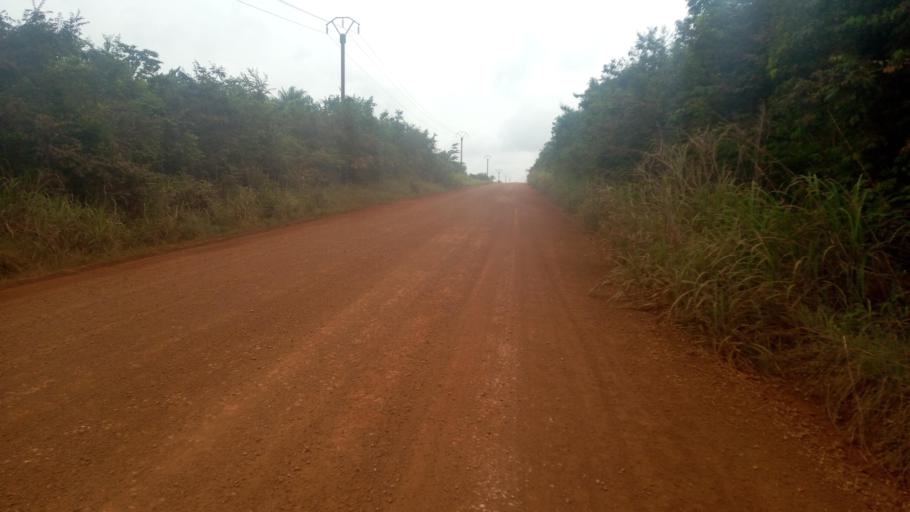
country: SL
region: Southern Province
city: Mogbwemo
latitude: 7.7124
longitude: -12.2850
